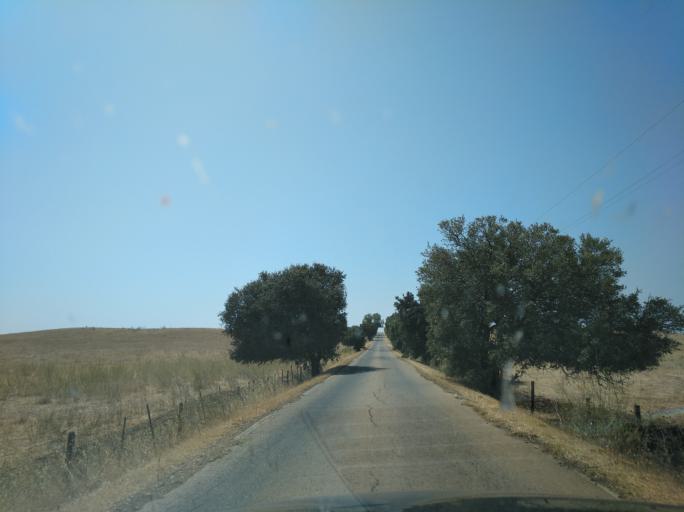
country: PT
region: Portalegre
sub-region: Campo Maior
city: Campo Maior
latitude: 39.0095
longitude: -6.9829
